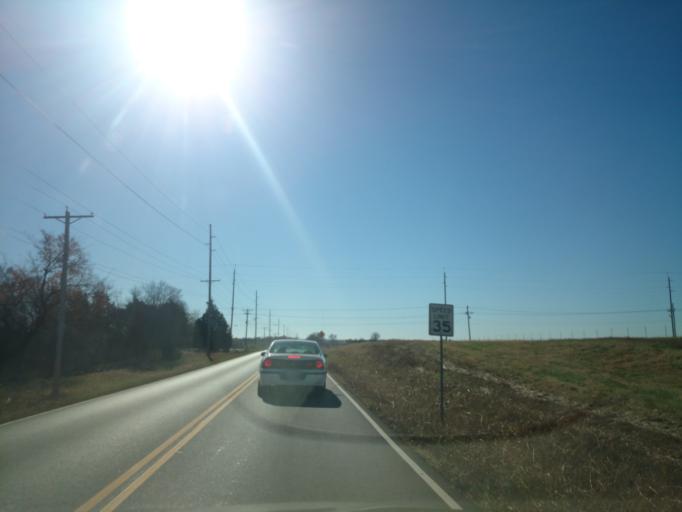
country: US
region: Oklahoma
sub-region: Payne County
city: Stillwater
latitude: 36.1319
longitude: -97.0873
